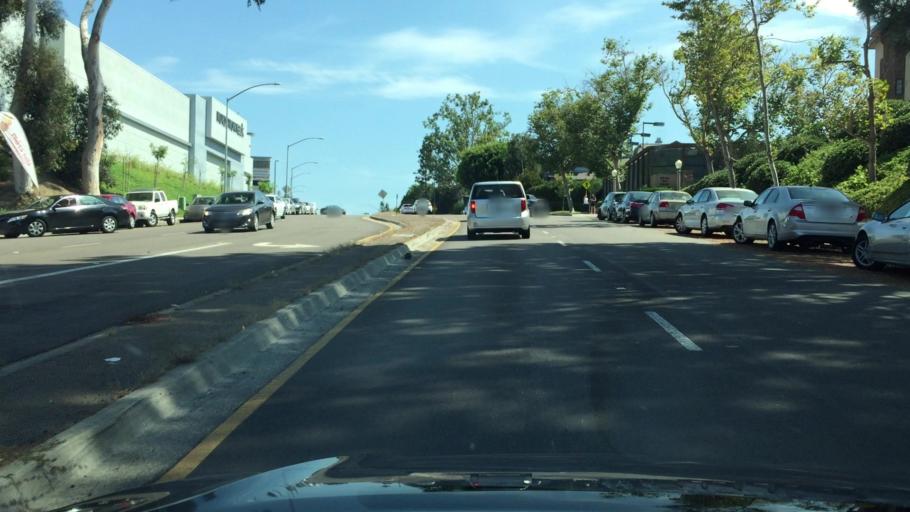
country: US
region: California
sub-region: San Diego County
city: La Jolla
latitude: 32.8702
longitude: -117.2339
